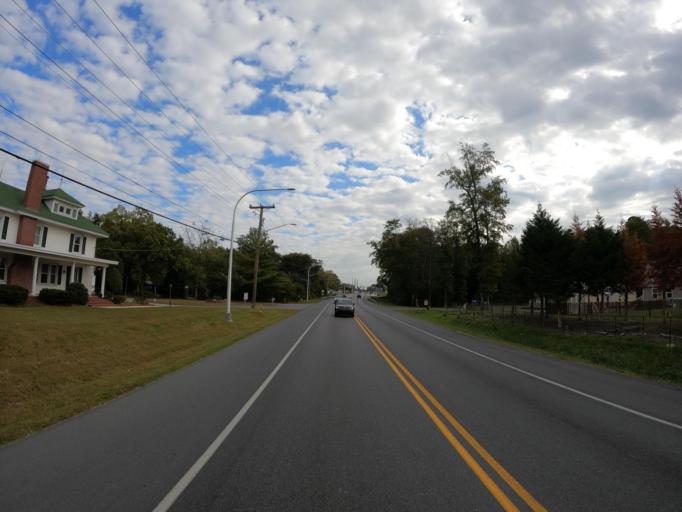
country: US
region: Delaware
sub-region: Sussex County
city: Milton
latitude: 38.7244
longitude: -75.2890
